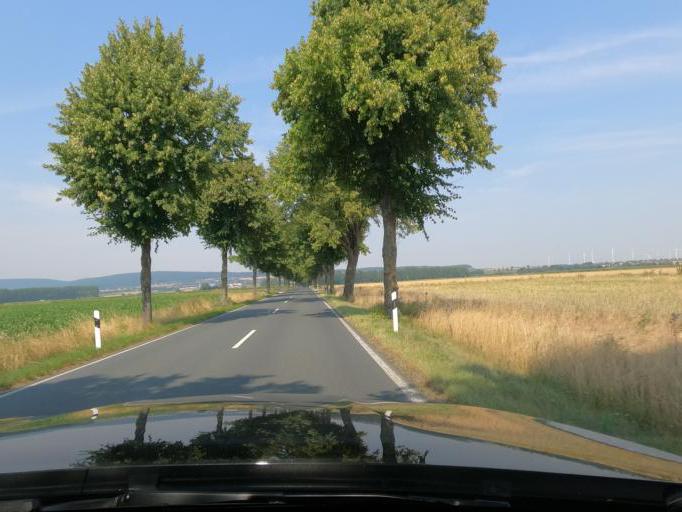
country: DE
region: Lower Saxony
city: Springe
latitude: 52.1854
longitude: 9.6384
